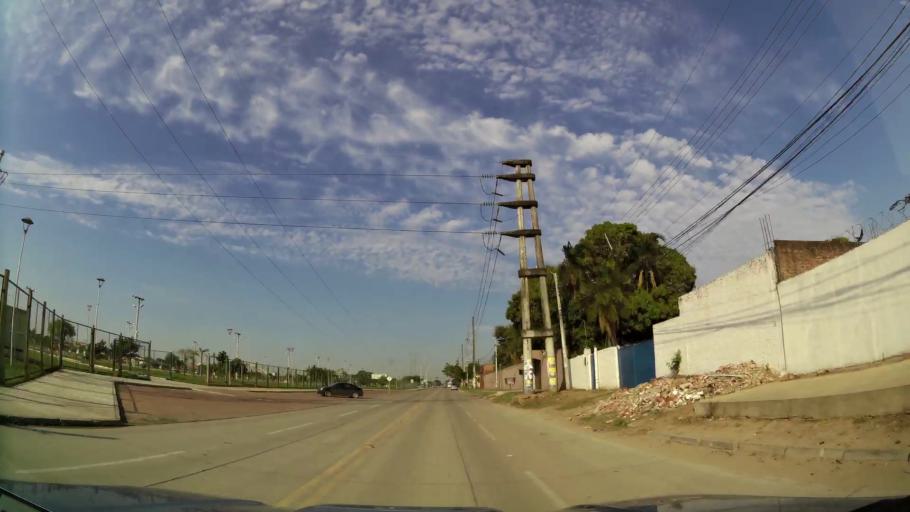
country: BO
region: Santa Cruz
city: Santa Cruz de la Sierra
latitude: -17.7467
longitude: -63.1495
